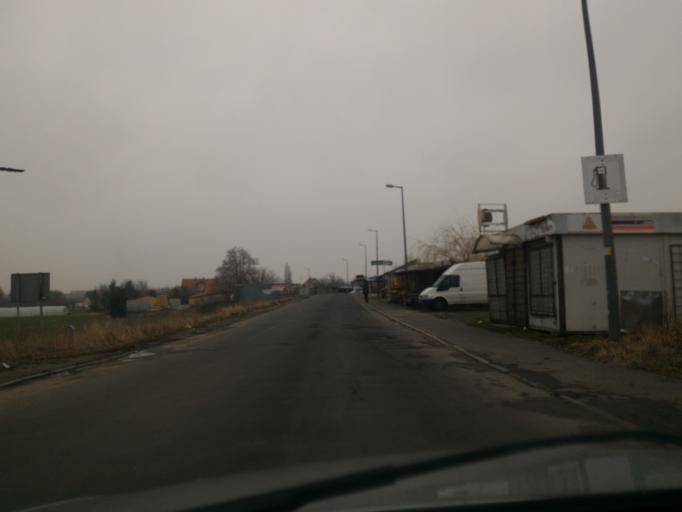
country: DE
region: Saxony
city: Zittau
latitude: 50.8963
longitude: 14.8373
